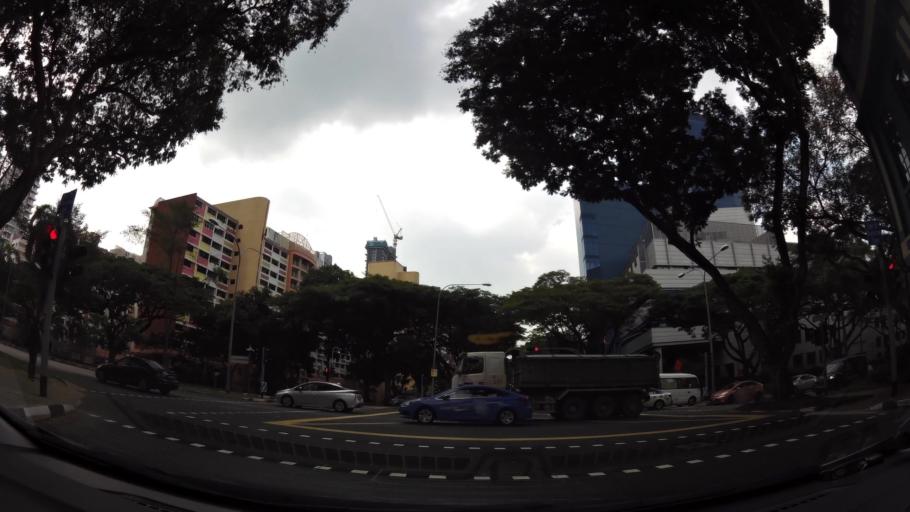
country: SG
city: Singapore
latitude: 1.2780
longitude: 103.8407
